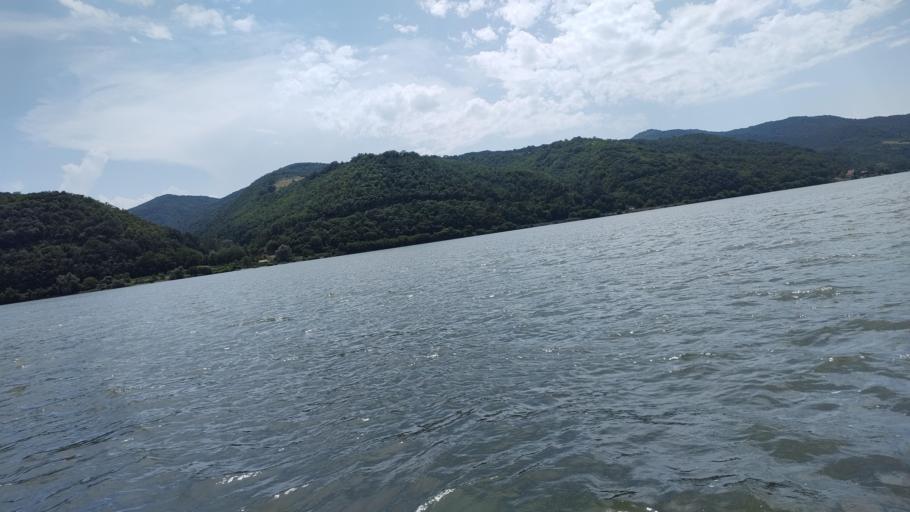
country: RO
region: Caras-Severin
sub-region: Comuna Berzasca
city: Berzasca
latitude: 44.6435
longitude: 21.9325
